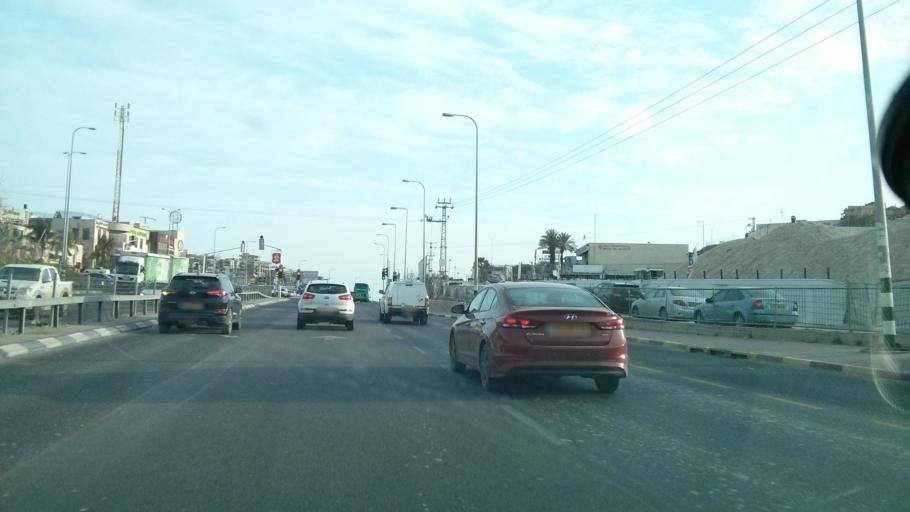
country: IL
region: Haifa
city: Umm el Fahm
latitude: 32.5335
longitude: 35.1480
